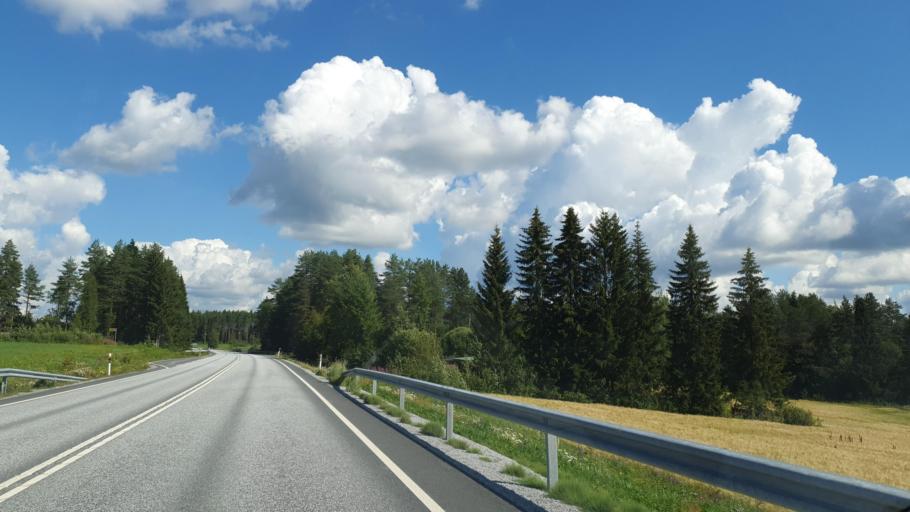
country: FI
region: Northern Savo
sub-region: Ylae-Savo
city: Sonkajaervi
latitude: 63.8416
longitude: 27.4319
